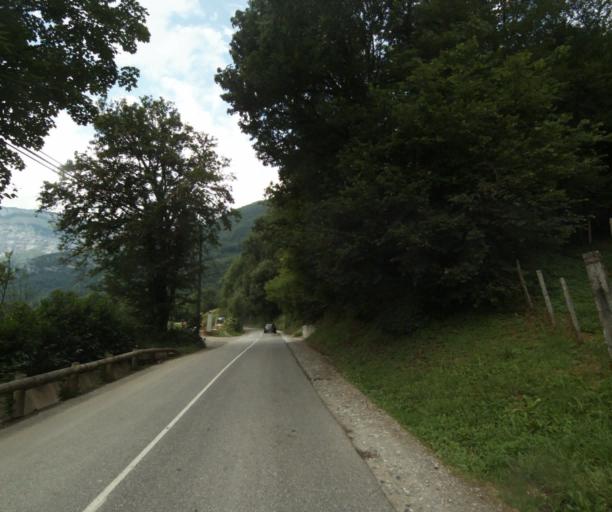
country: FR
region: Rhone-Alpes
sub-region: Departement de la Haute-Savoie
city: Thones
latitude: 45.8948
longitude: 6.3086
